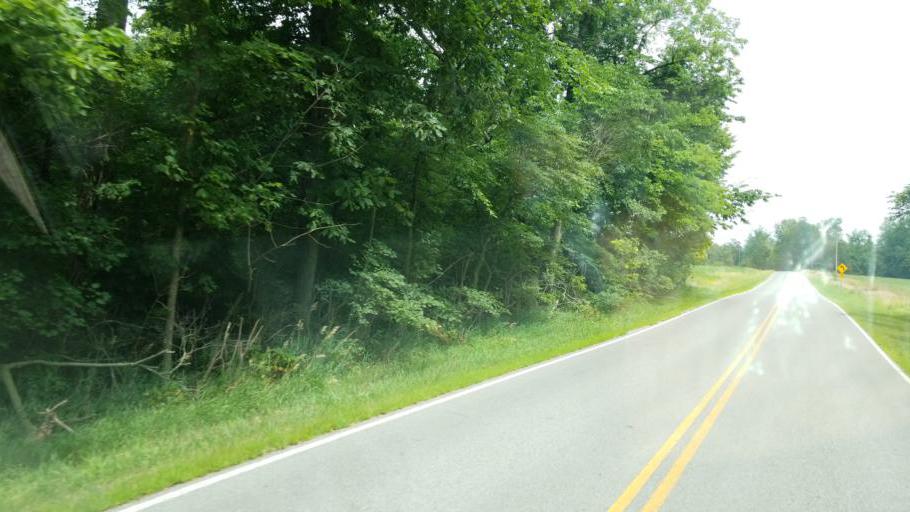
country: US
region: Ohio
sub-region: Logan County
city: Bellefontaine
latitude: 40.4128
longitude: -83.7791
